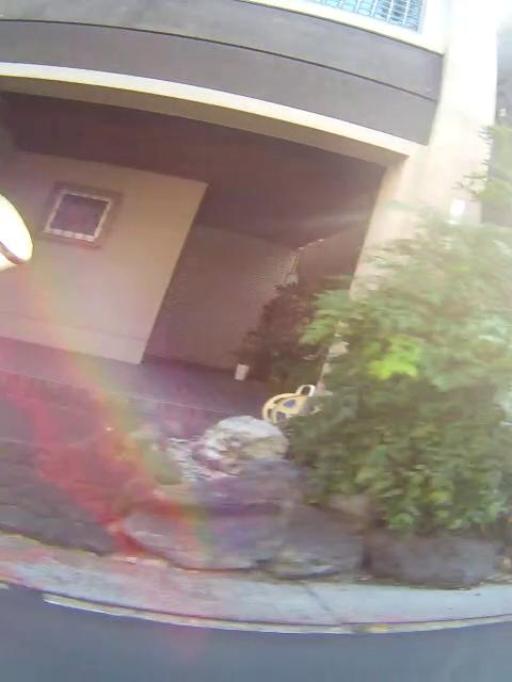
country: JP
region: Osaka
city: Yao
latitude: 34.6577
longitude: 135.6398
